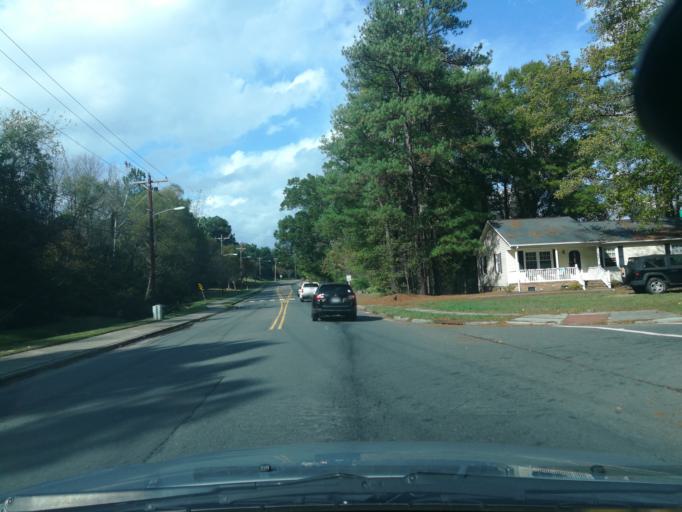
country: US
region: North Carolina
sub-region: Durham County
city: Durham
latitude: 36.0441
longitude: -78.9353
